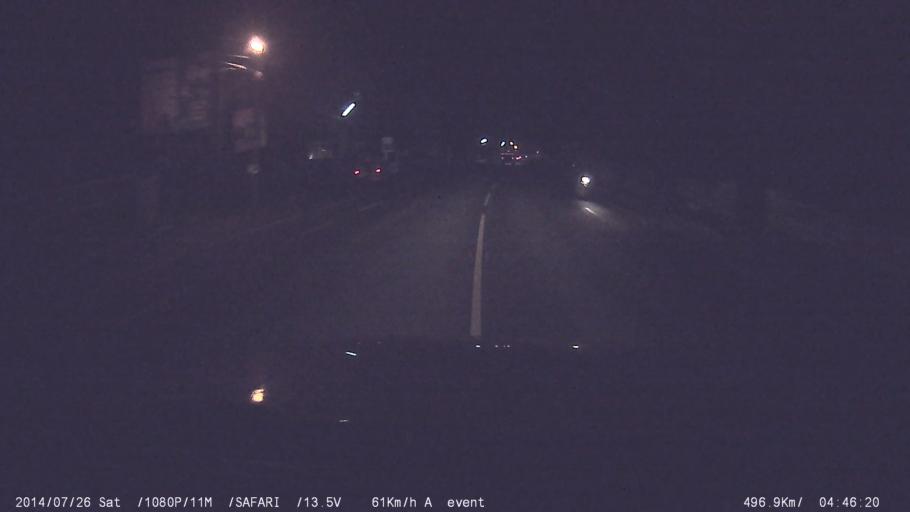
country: IN
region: Kerala
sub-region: Ernakulam
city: Angamali
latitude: 10.1832
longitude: 76.4096
